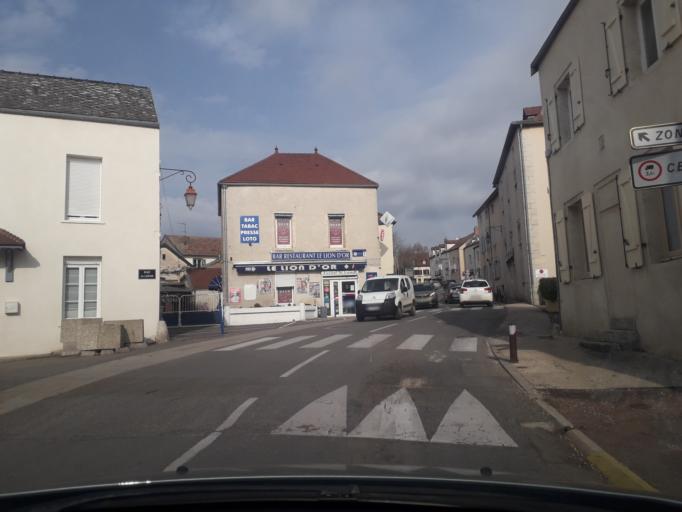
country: FR
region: Bourgogne
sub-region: Departement de la Cote-d'Or
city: Messigny-et-Vantoux
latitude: 47.4054
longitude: 5.0176
